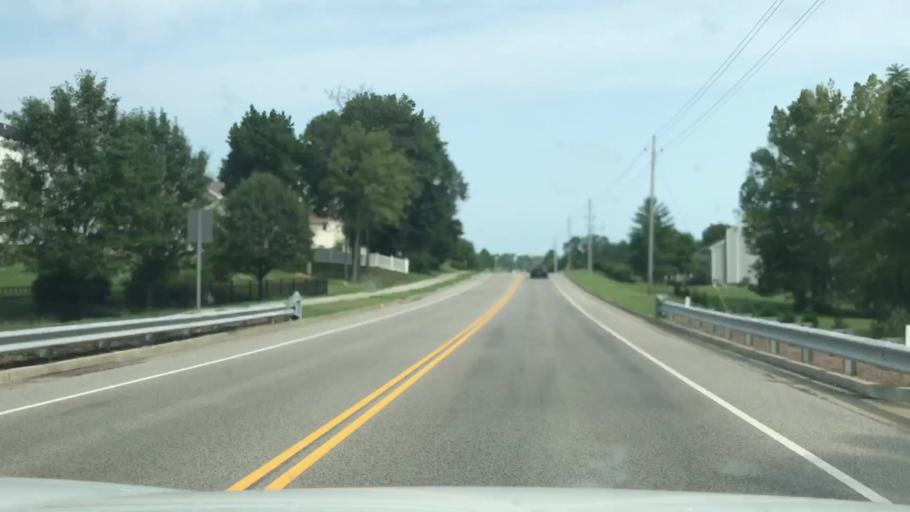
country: US
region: Missouri
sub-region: Saint Charles County
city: Cottleville
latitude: 38.7218
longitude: -90.6426
